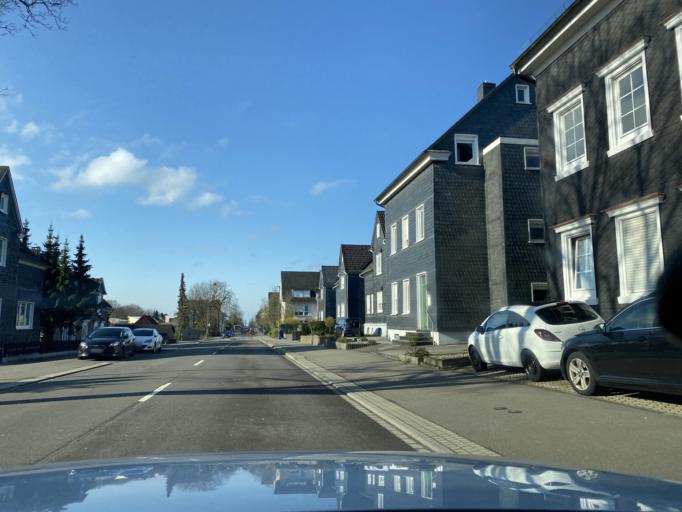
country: DE
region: North Rhine-Westphalia
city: Wermelskirchen
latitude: 51.1275
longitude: 7.1976
